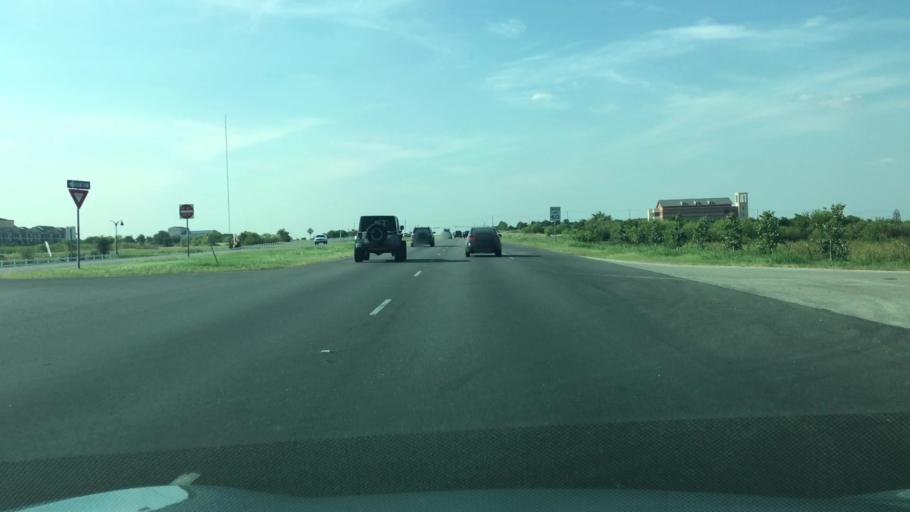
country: US
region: Texas
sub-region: Hays County
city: Kyle
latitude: 30.0211
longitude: -97.8721
